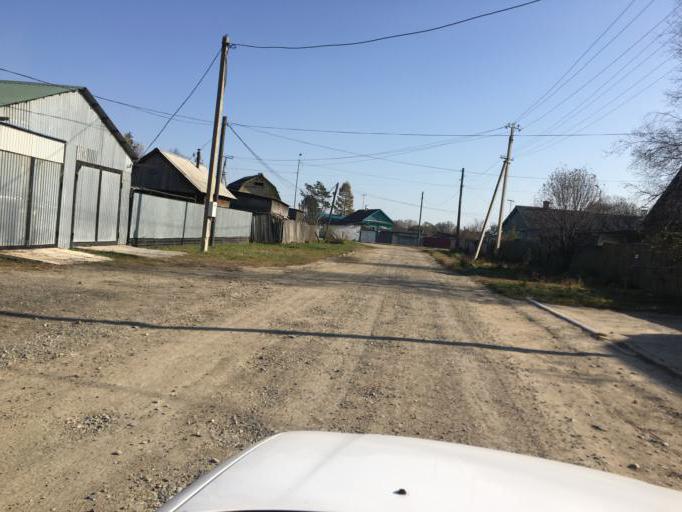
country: RU
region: Primorskiy
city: Dal'nerechensk
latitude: 45.9205
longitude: 133.7225
